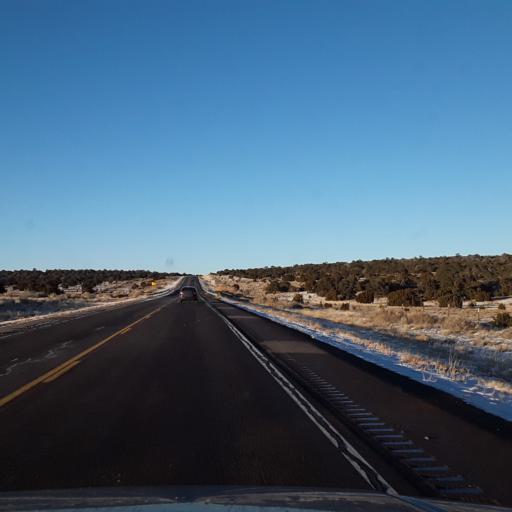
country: US
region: New Mexico
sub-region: Lincoln County
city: Carrizozo
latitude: 34.2110
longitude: -105.6481
